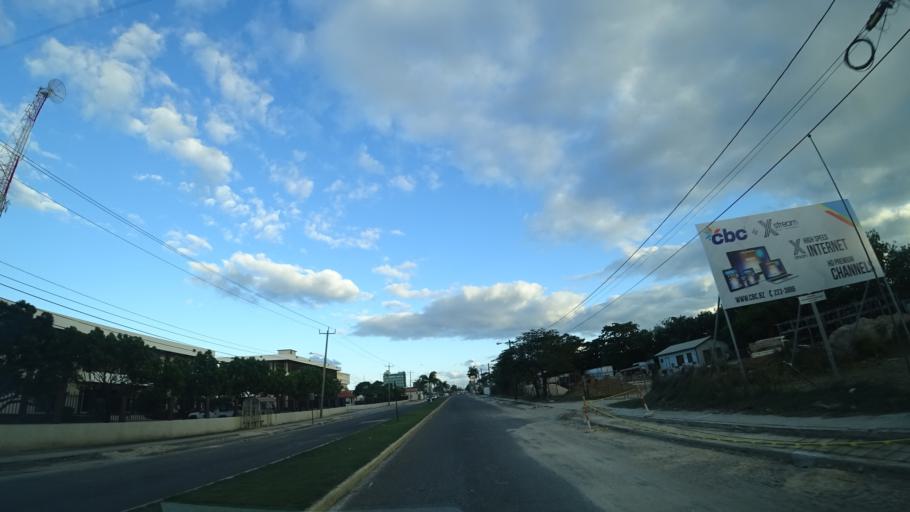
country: BZ
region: Belize
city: Belize City
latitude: 17.5100
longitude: -88.2104
